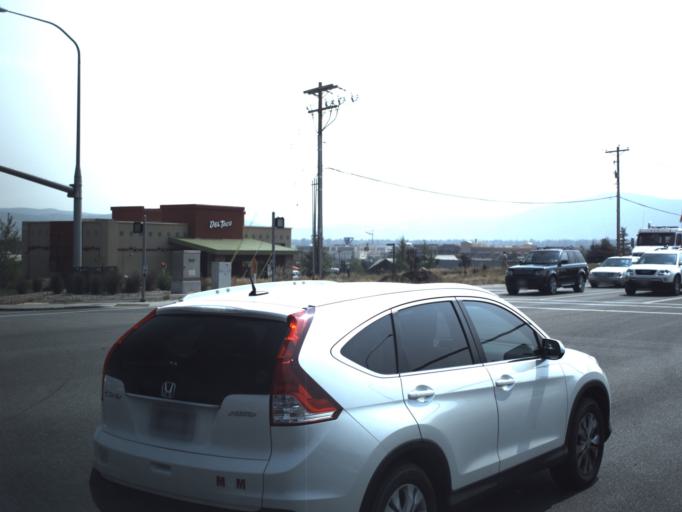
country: US
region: Utah
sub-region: Summit County
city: Snyderville
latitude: 40.7246
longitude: -111.5448
